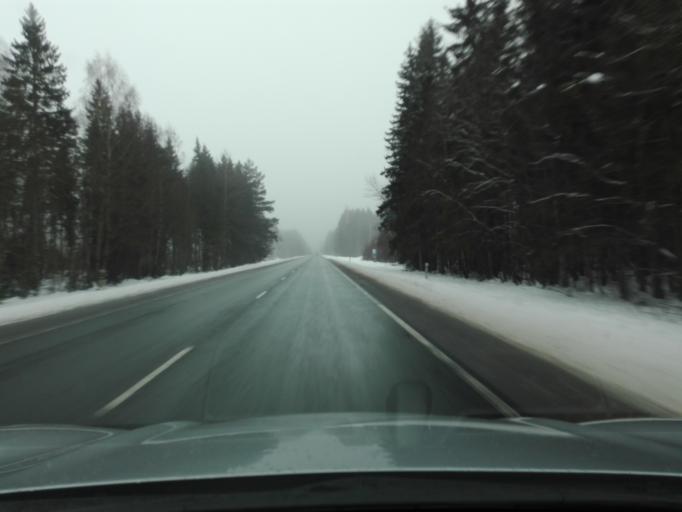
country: EE
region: Raplamaa
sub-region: Kohila vald
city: Kohila
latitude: 59.1574
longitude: 24.7760
